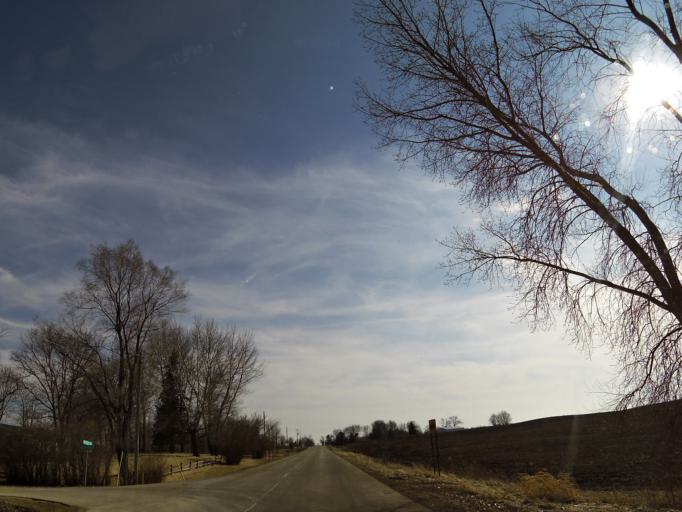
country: US
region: Minnesota
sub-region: Scott County
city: Prior Lake
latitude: 44.6819
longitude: -93.4808
